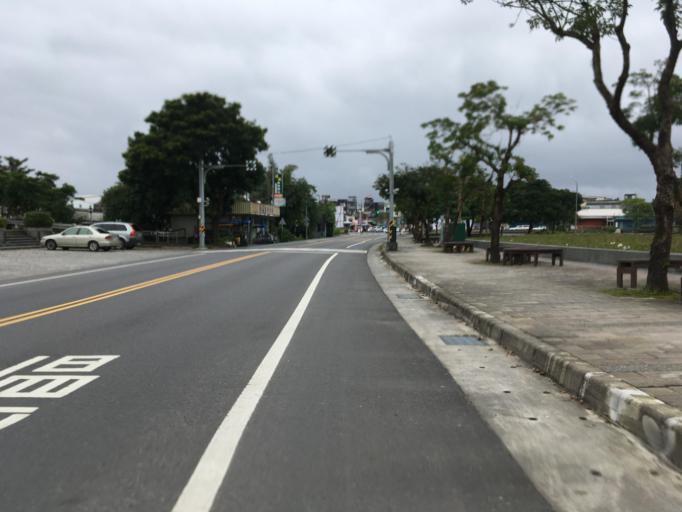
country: TW
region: Taiwan
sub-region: Yilan
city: Yilan
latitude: 24.6320
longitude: 121.7912
